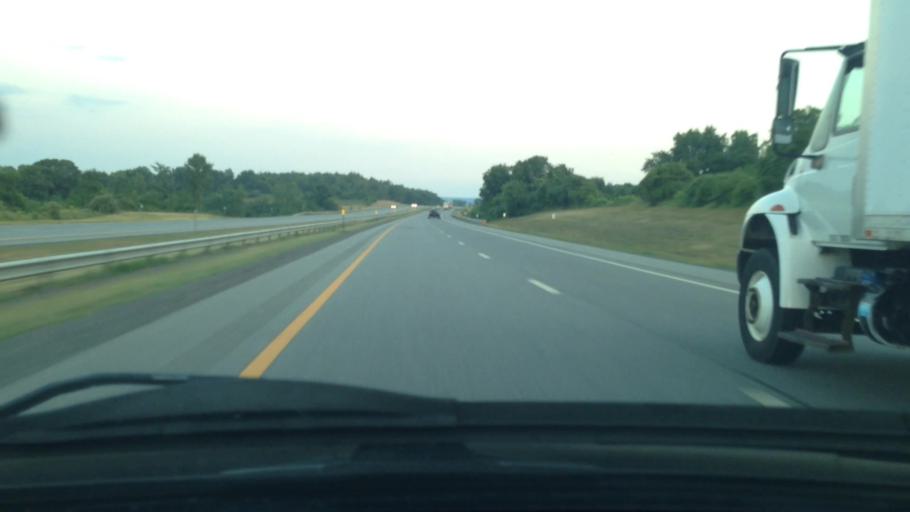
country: US
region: New York
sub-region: Montgomery County
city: Saint Johnsville
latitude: 42.9779
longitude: -74.6545
